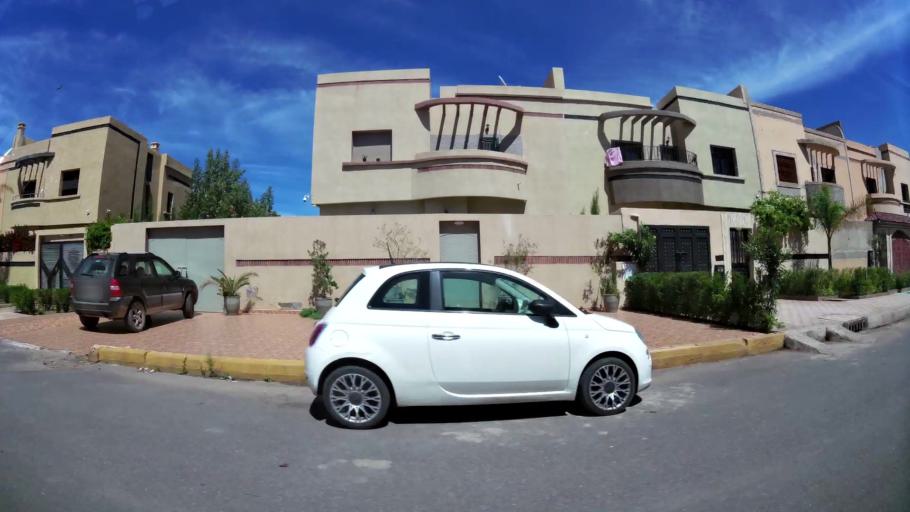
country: MA
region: Marrakech-Tensift-Al Haouz
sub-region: Marrakech
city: Marrakesh
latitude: 31.6464
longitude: -8.0717
